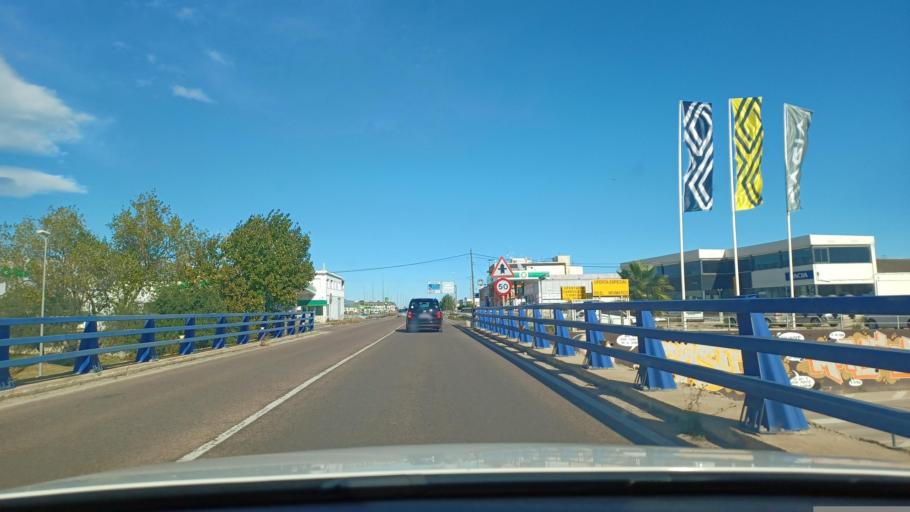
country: ES
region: Valencia
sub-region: Provincia de Castello
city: Vinaros
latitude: 40.4808
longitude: 0.4727
